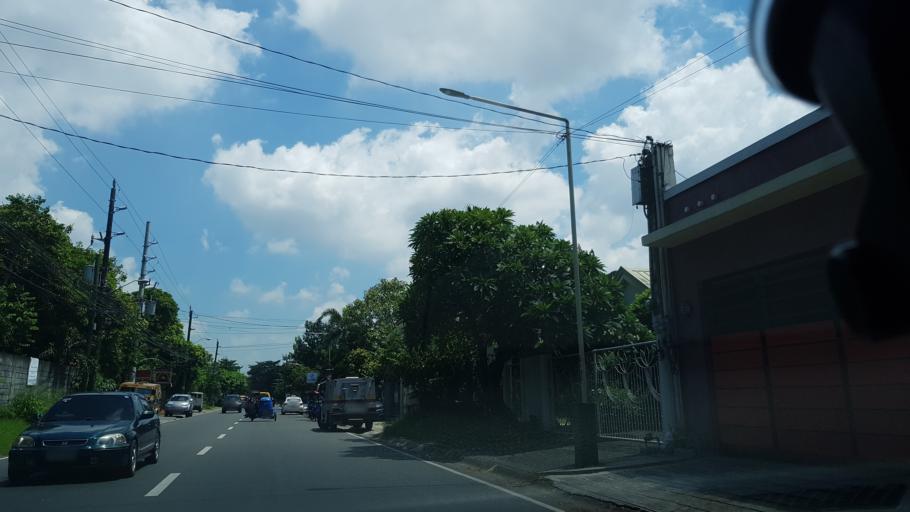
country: PH
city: Sambayanihan People's Village
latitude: 14.4495
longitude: 121.0068
